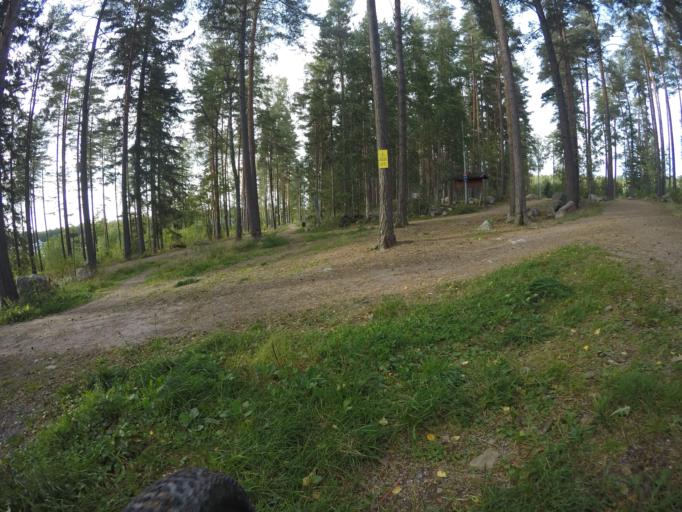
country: SE
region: Vaestmanland
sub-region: Kopings Kommun
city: Koping
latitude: 59.5252
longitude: 16.0004
